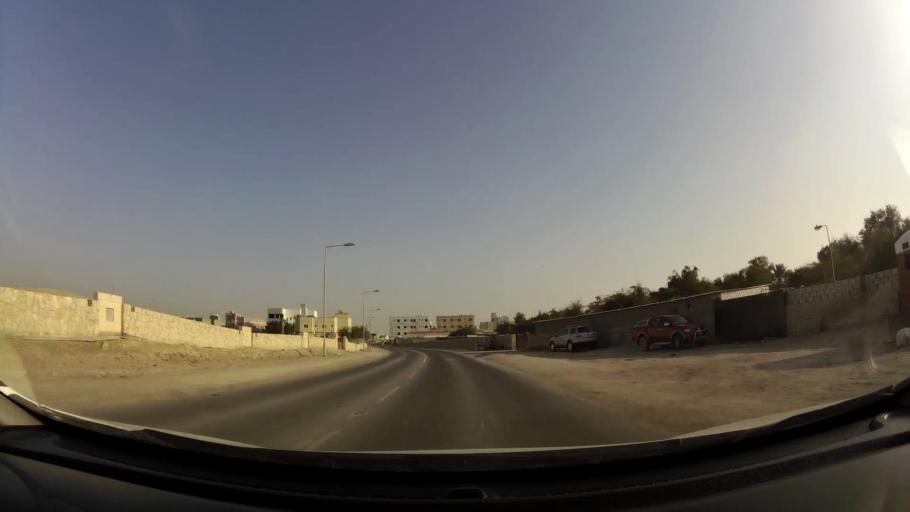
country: BH
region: Manama
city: Jidd Hafs
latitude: 26.2133
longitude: 50.5003
